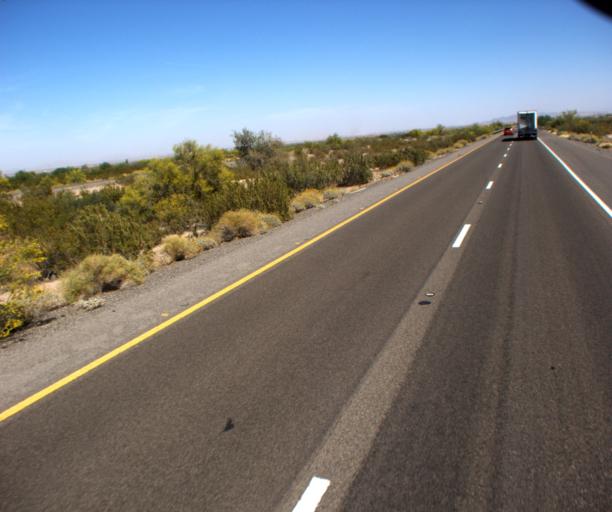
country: US
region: Arizona
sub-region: Pinal County
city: Casa Grande
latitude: 32.8284
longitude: -111.9832
